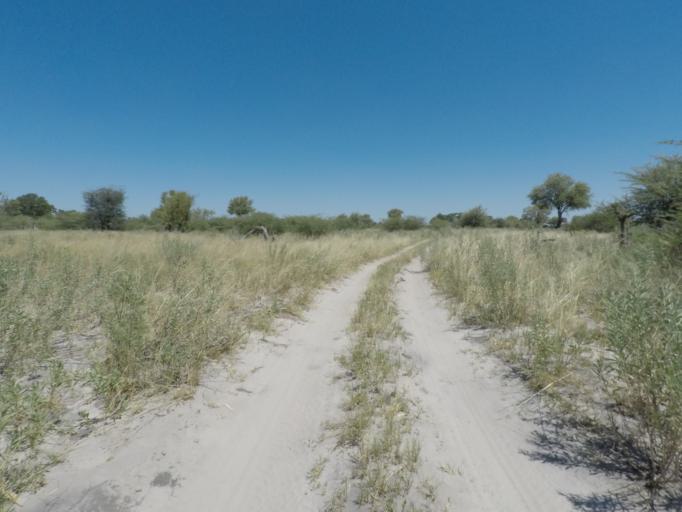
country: BW
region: North West
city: Maun
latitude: -19.4435
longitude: 23.5594
